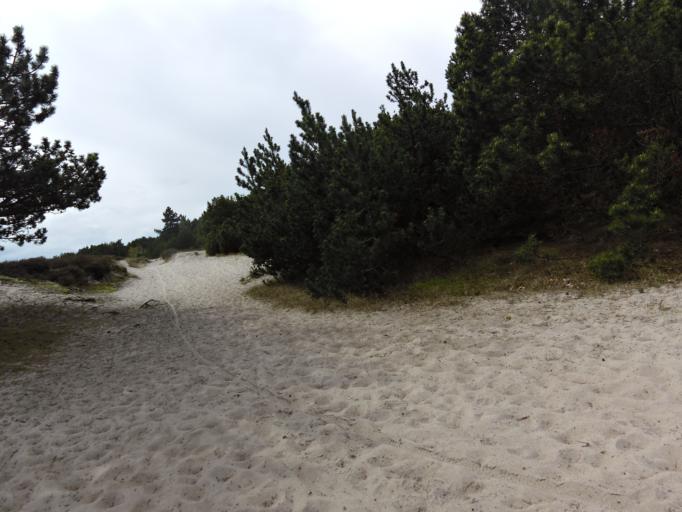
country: DE
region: Mecklenburg-Vorpommern
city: Hiddensee
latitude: 54.5424
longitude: 13.0922
